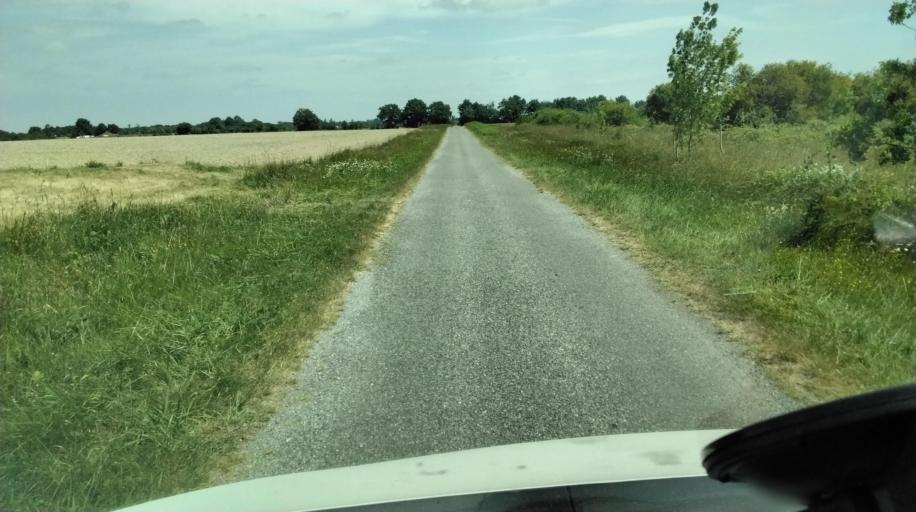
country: FR
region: Midi-Pyrenees
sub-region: Departement de la Haute-Garonne
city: Rieumes
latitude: 43.4009
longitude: 1.0966
